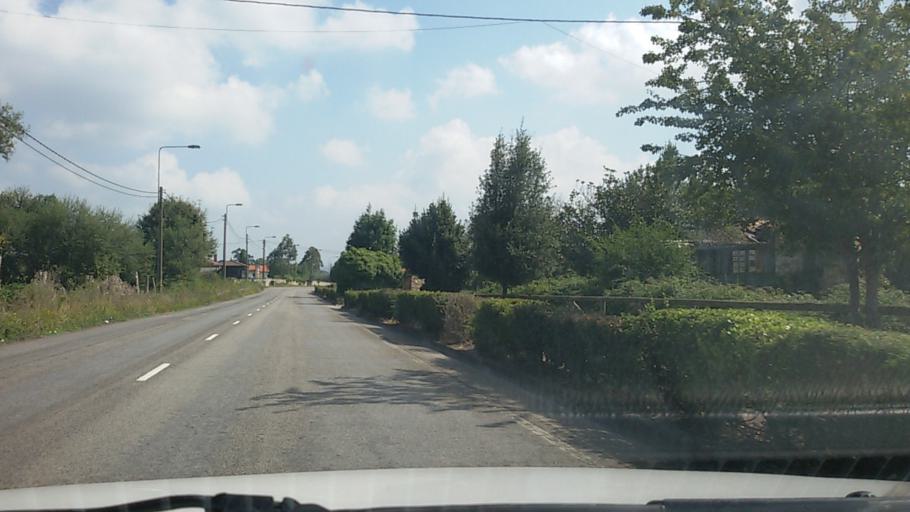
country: ES
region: Asturias
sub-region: Province of Asturias
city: Lugones
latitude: 43.4387
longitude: -5.8366
